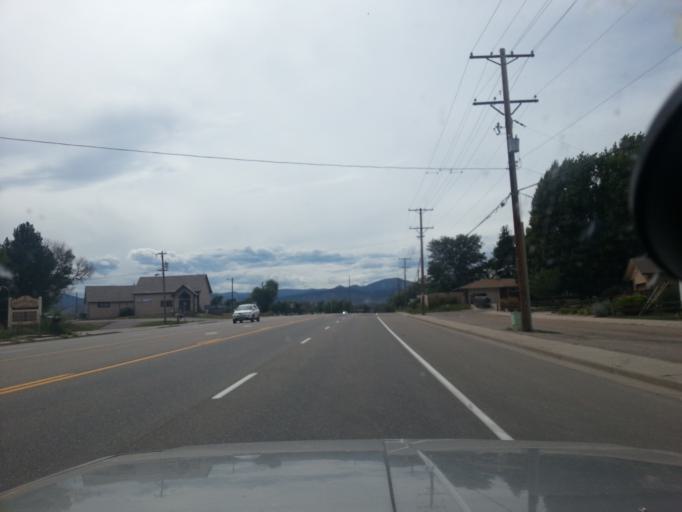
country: US
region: Colorado
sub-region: Larimer County
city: Loveland
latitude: 40.4073
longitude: -105.1233
